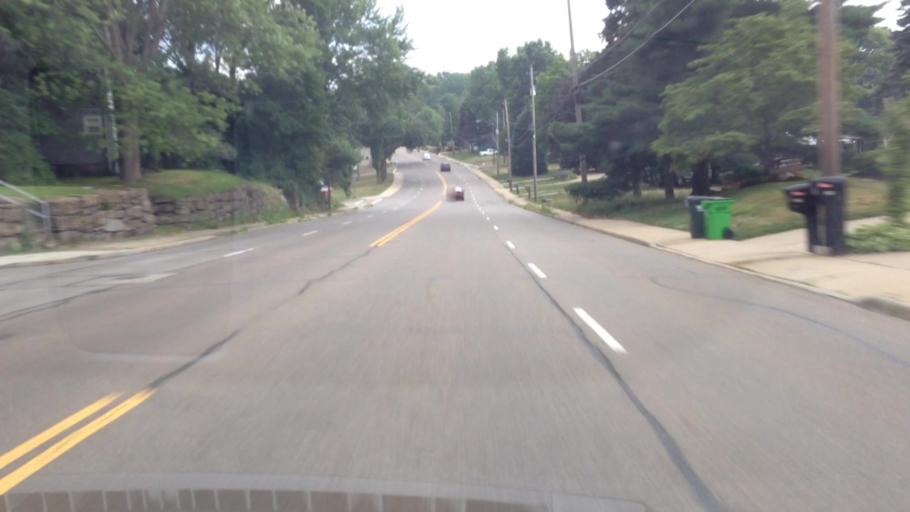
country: US
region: Ohio
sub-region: Summit County
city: Barberton
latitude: 41.0361
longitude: -81.5854
